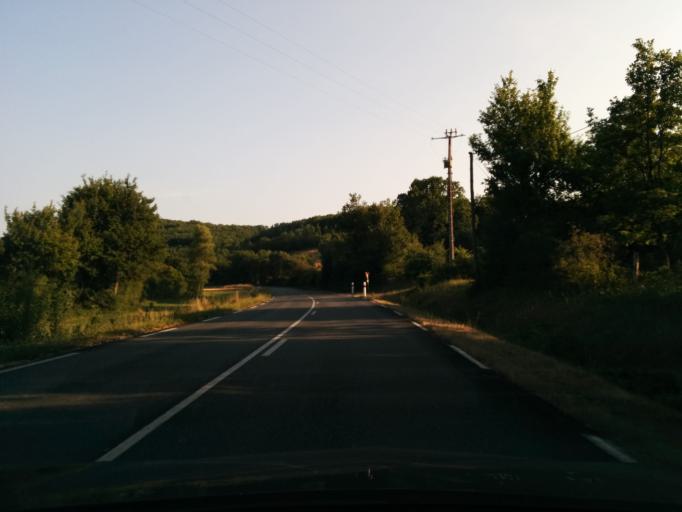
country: FR
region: Midi-Pyrenees
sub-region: Departement du Lot
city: Le Vigan
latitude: 44.7022
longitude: 1.4797
